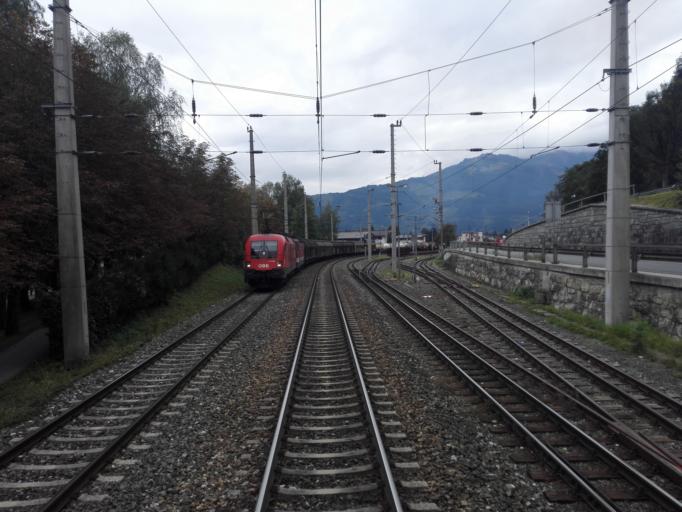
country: AT
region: Salzburg
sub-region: Politischer Bezirk Zell am See
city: Zell am See
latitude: 47.3128
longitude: 12.7946
